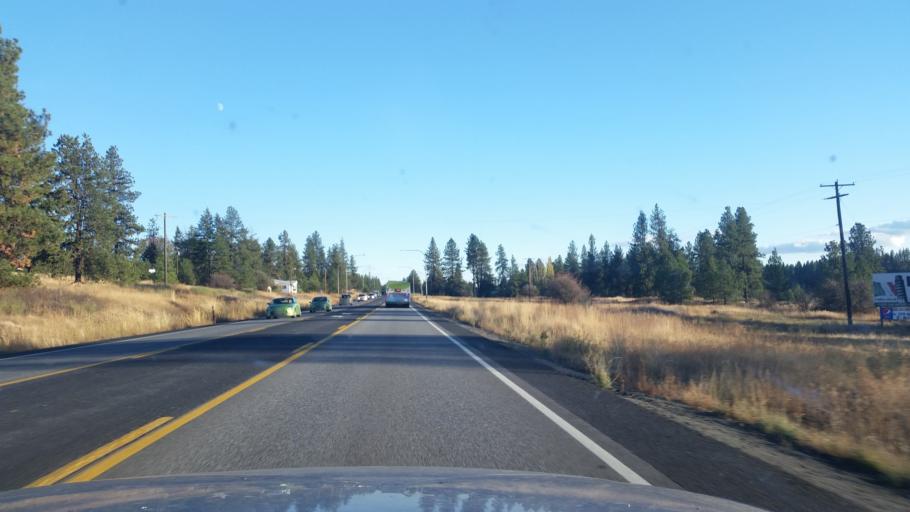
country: US
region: Washington
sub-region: Spokane County
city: Cheney
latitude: 47.5471
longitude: -117.5864
